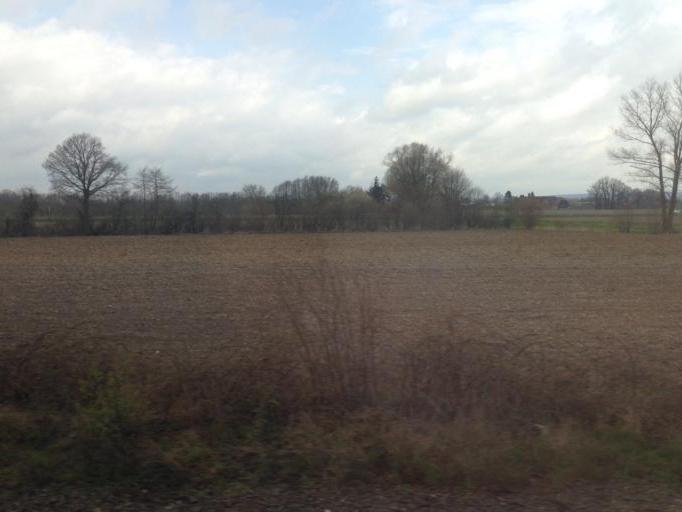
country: DE
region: North Rhine-Westphalia
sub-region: Regierungsbezirk Munster
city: Nottuln
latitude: 51.8875
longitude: 7.4140
